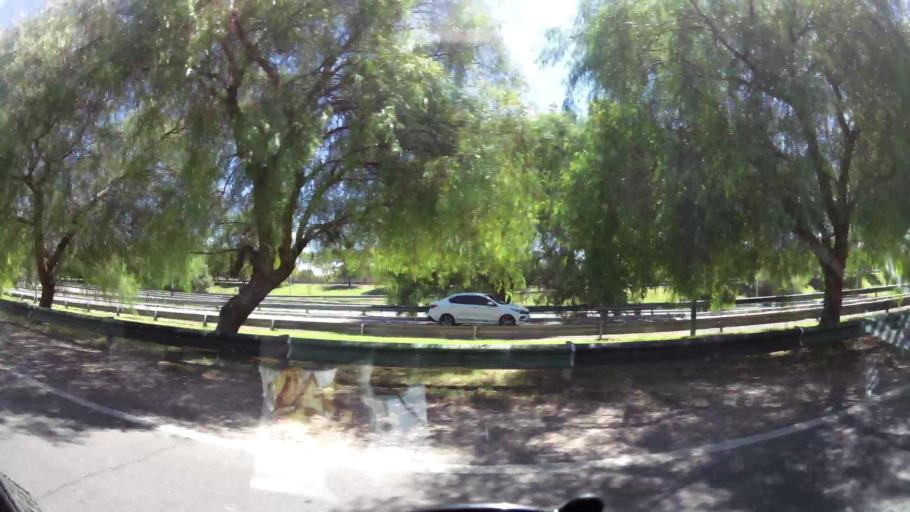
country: AR
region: San Juan
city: San Juan
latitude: -31.5179
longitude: -68.5302
